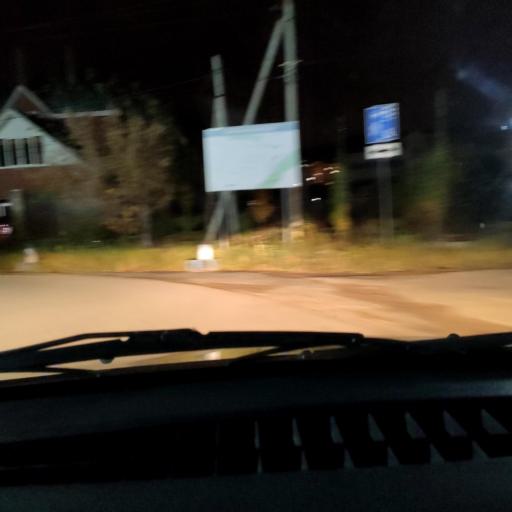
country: RU
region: Bashkortostan
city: Ufa
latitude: 54.6923
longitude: 55.9781
